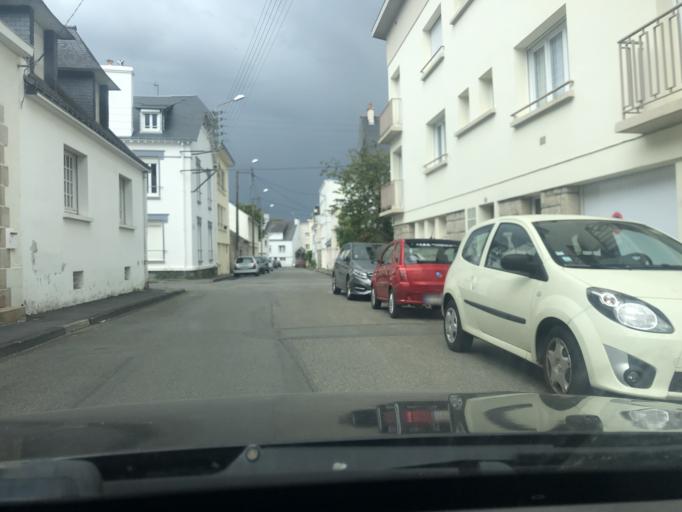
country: FR
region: Brittany
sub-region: Departement du Morbihan
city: Lorient
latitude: 47.7432
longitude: -3.3748
